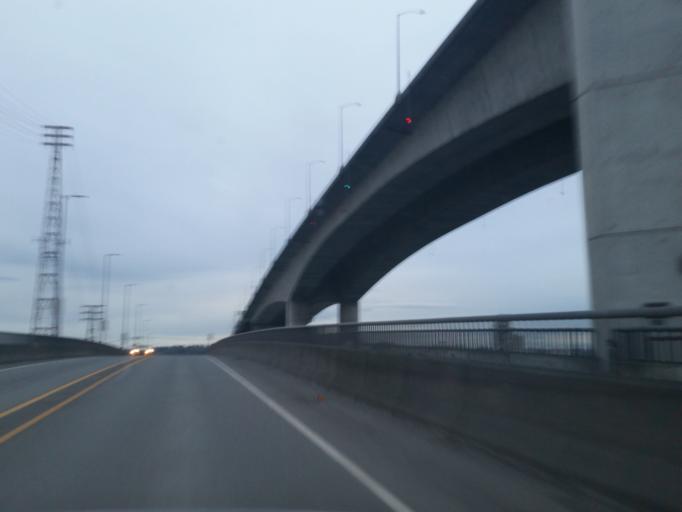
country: US
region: Washington
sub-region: King County
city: Seattle
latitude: 47.5714
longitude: -122.3548
